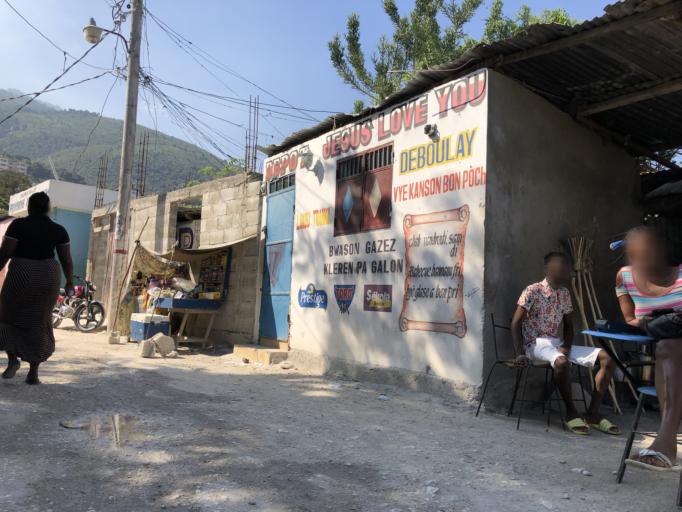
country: HT
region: Ouest
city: Port-au-Prince
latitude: 18.5226
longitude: -72.3229
